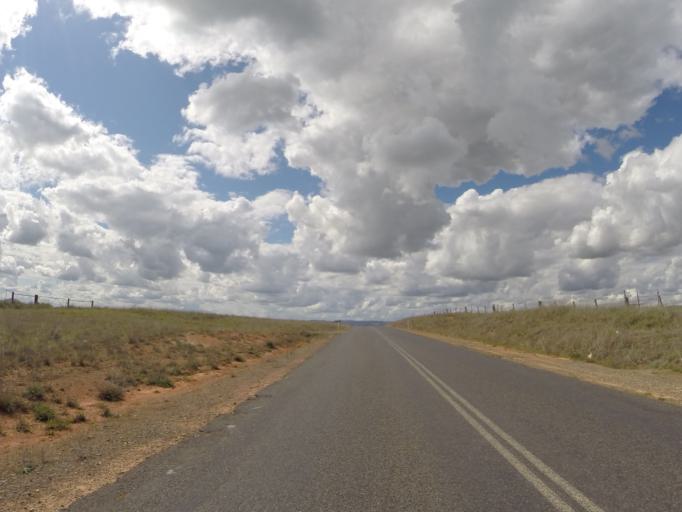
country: AU
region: New South Wales
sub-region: Yass Valley
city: Yass
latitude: -34.9074
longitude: 148.8869
